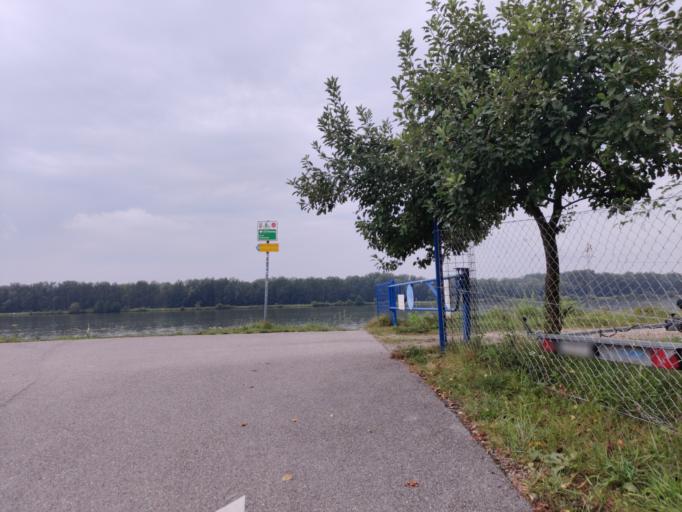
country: AT
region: Upper Austria
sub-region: Politischer Bezirk Urfahr-Umgebung
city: Steyregg
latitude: 48.2692
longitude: 14.3852
